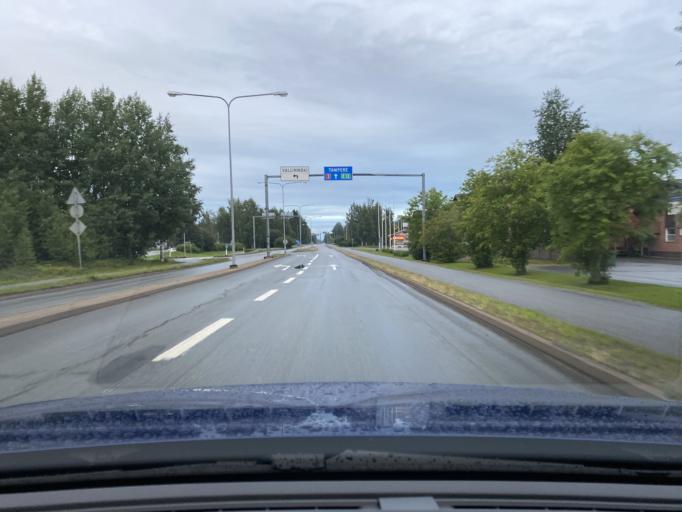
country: FI
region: Ostrobothnia
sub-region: Kyroenmaa
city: Laihia
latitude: 62.9807
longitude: 22.0078
